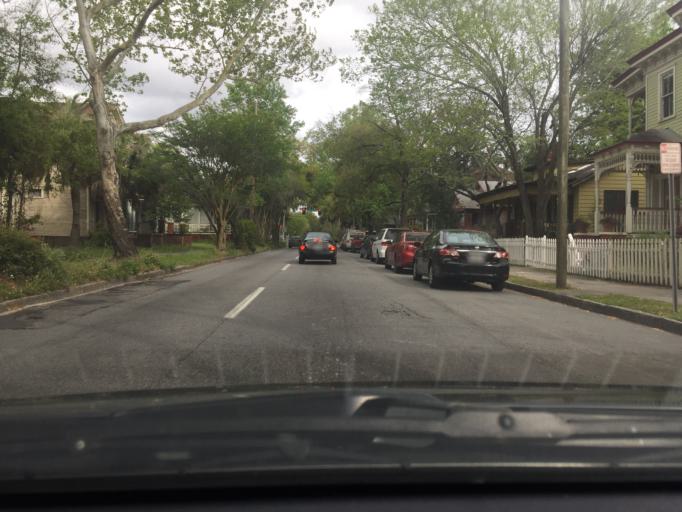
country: US
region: Georgia
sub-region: Chatham County
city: Savannah
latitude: 32.0590
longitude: -81.0853
